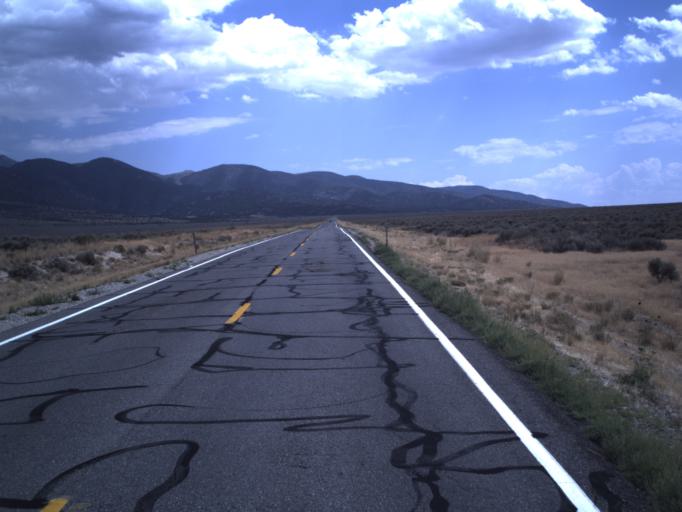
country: US
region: Utah
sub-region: Tooele County
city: Tooele
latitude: 40.3702
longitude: -112.3559
